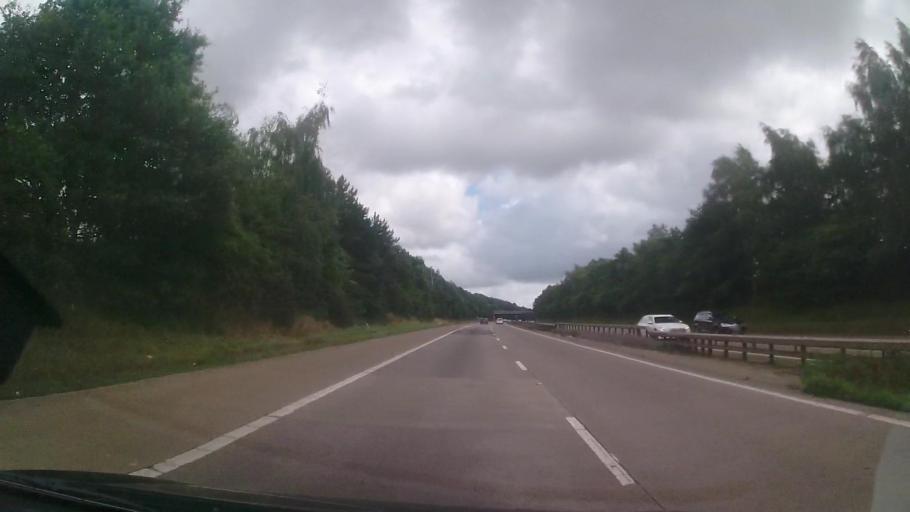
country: GB
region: England
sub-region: Shropshire
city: Albrighton
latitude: 52.6489
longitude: -2.2388
